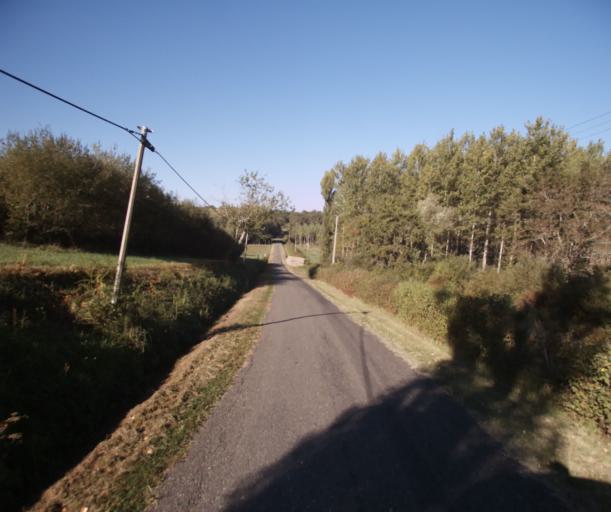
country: FR
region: Midi-Pyrenees
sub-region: Departement du Gers
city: Cazaubon
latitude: 43.9102
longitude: -0.0078
